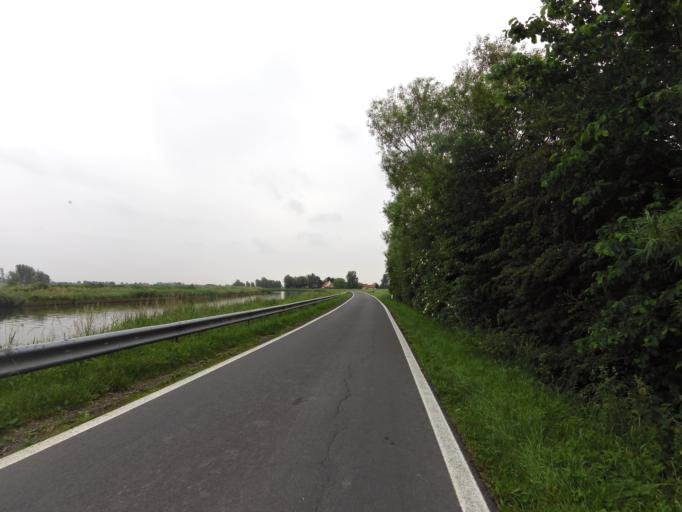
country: BE
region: Flanders
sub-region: Provincie West-Vlaanderen
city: Diksmuide
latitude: 51.0978
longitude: 2.8230
